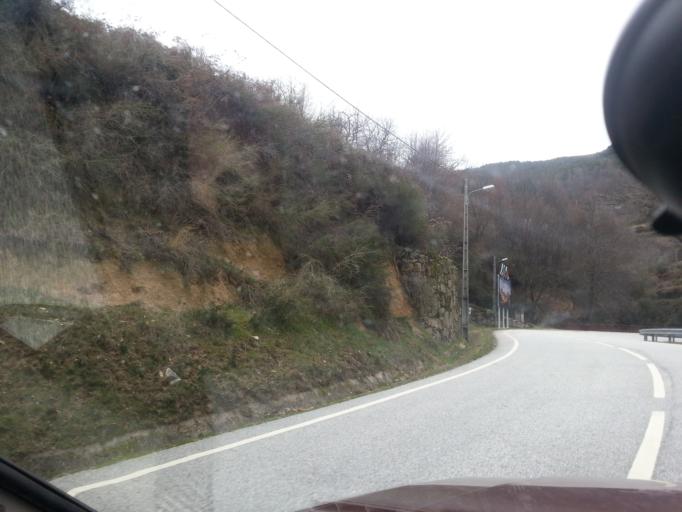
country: PT
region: Guarda
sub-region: Manteigas
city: Manteigas
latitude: 40.4058
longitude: -7.5347
